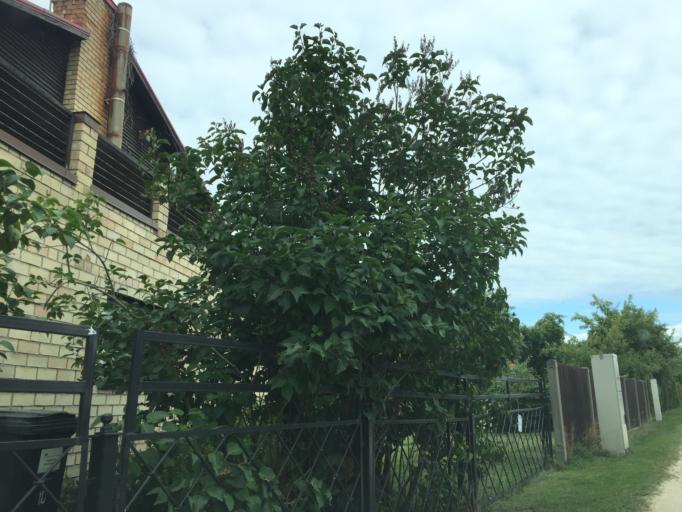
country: LV
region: Riga
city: Jaunciems
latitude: 57.1022
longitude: 24.1886
